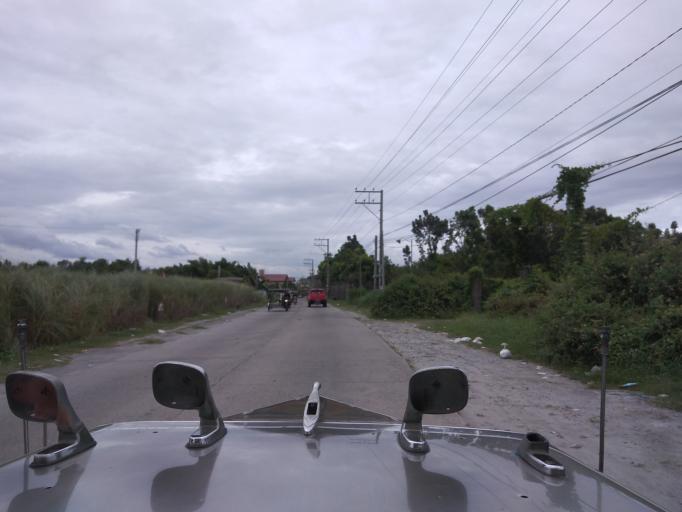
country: PH
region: Central Luzon
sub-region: Province of Pampanga
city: Pandacaqui
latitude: 15.1869
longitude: 120.6397
